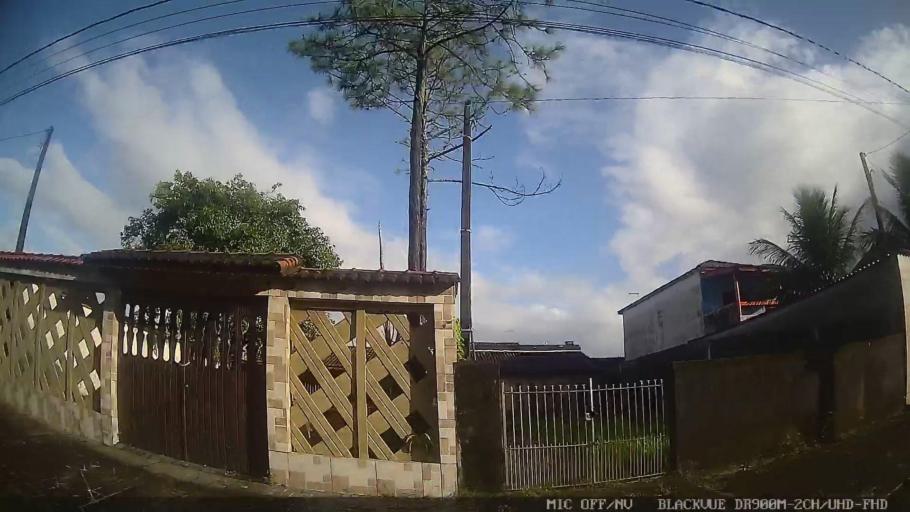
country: BR
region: Sao Paulo
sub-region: Itanhaem
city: Itanhaem
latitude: -24.2405
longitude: -46.8931
